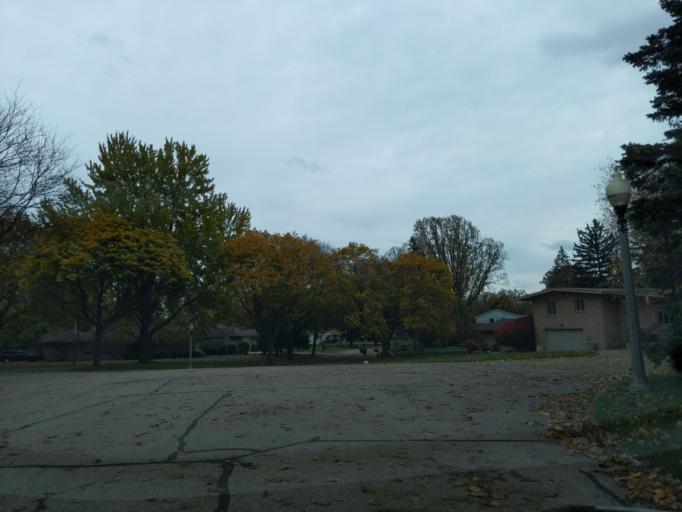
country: US
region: Michigan
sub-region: Ingham County
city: Edgemont Park
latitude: 42.7143
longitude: -84.5902
